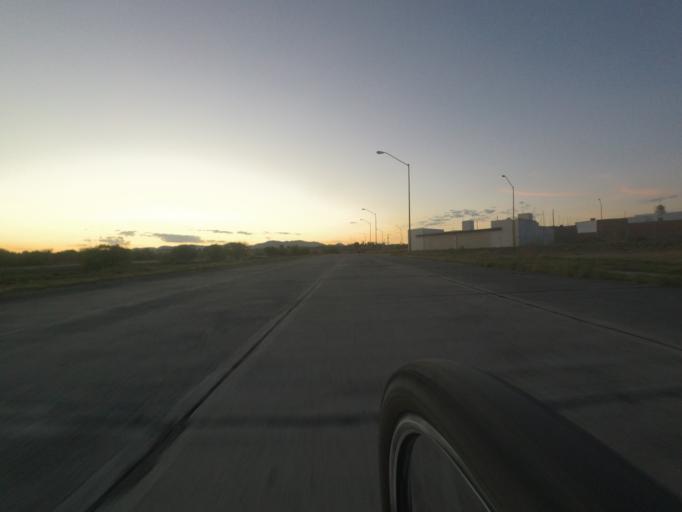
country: MX
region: Aguascalientes
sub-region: Aguascalientes
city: La Loma de los Negritos
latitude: 21.8479
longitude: -102.3325
